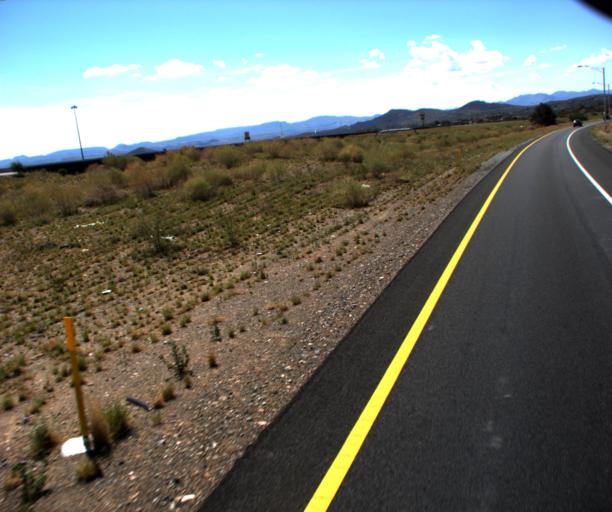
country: US
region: Arizona
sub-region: Yavapai County
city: Cordes Lakes
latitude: 34.3298
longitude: -112.1231
